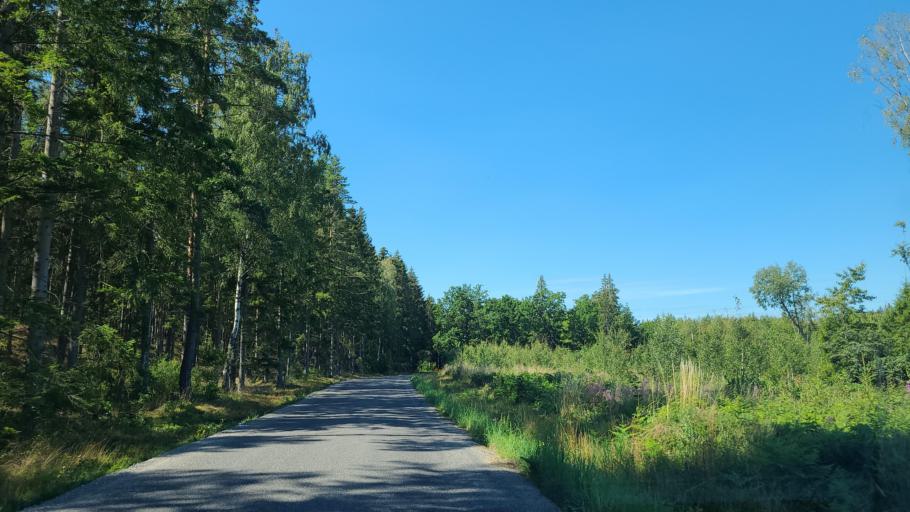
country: SE
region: Kalmar
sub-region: Kalmar Kommun
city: Ljungbyholm
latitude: 56.5690
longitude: 16.0639
